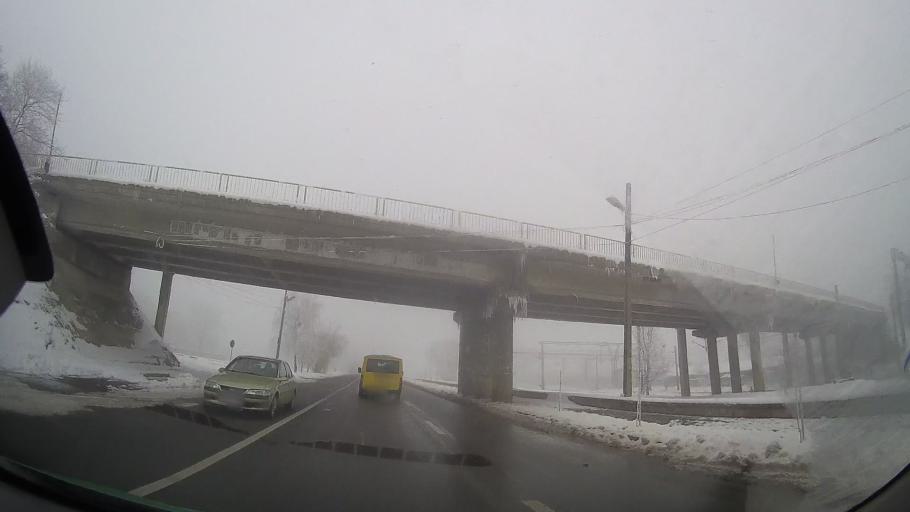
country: RO
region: Iasi
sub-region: Municipiul Pascani
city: Pascani
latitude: 47.2444
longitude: 26.7312
